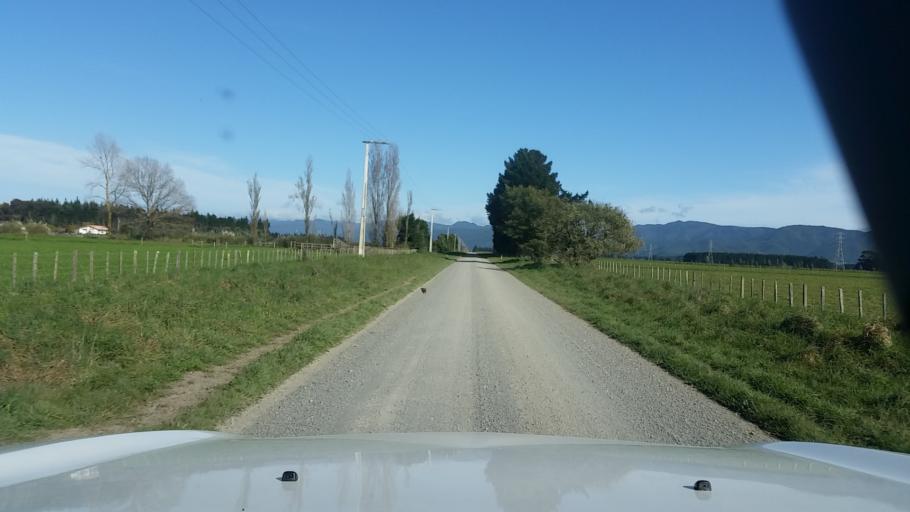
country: NZ
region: Wellington
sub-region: Masterton District
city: Masterton
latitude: -41.1189
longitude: 175.4157
